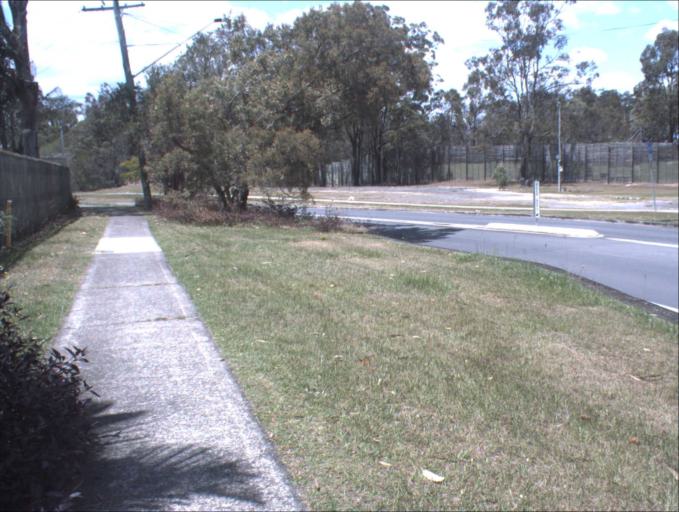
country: AU
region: Queensland
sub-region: Logan
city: Slacks Creek
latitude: -27.6525
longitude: 153.1626
